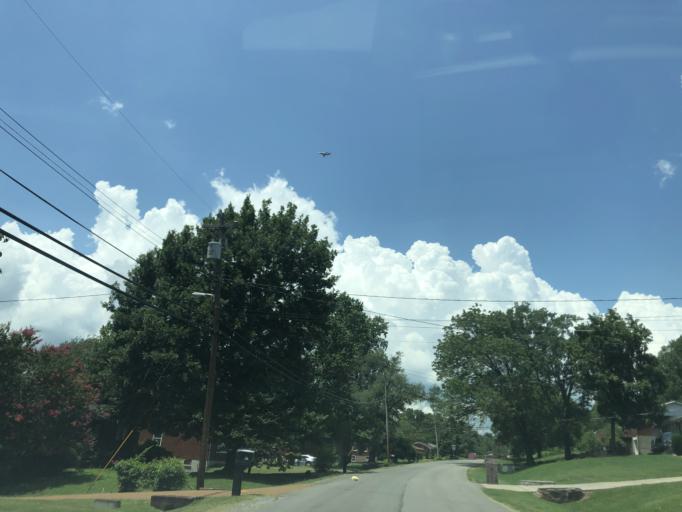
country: US
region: Tennessee
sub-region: Davidson County
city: Lakewood
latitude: 36.1961
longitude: -86.6252
